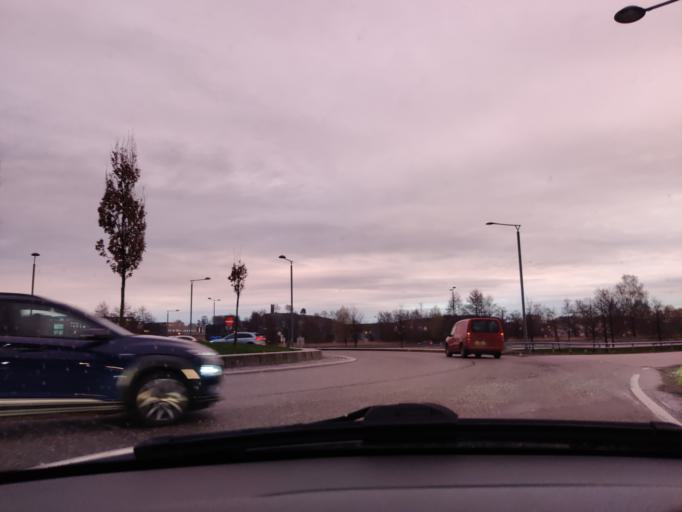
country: NO
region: Vestfold
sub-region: Tonsberg
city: Tonsberg
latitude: 59.2816
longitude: 10.3985
